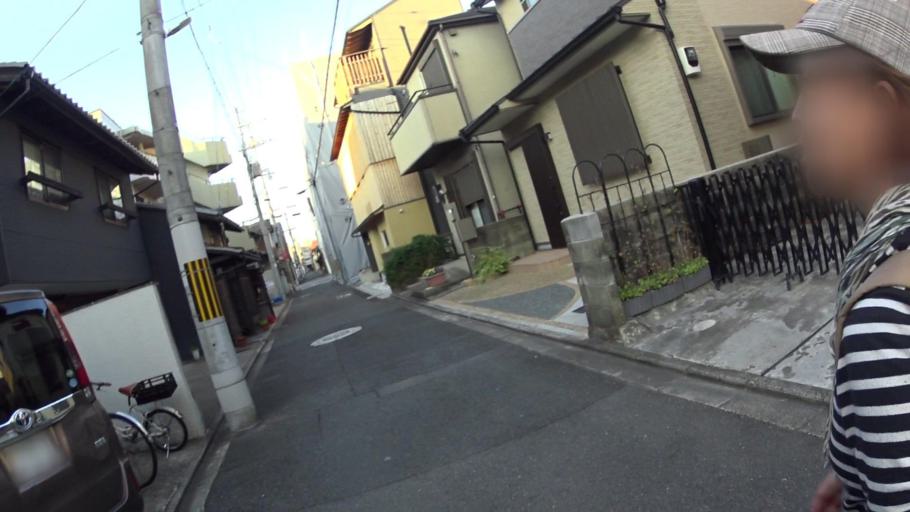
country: JP
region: Kyoto
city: Kyoto
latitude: 35.0242
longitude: 135.7494
